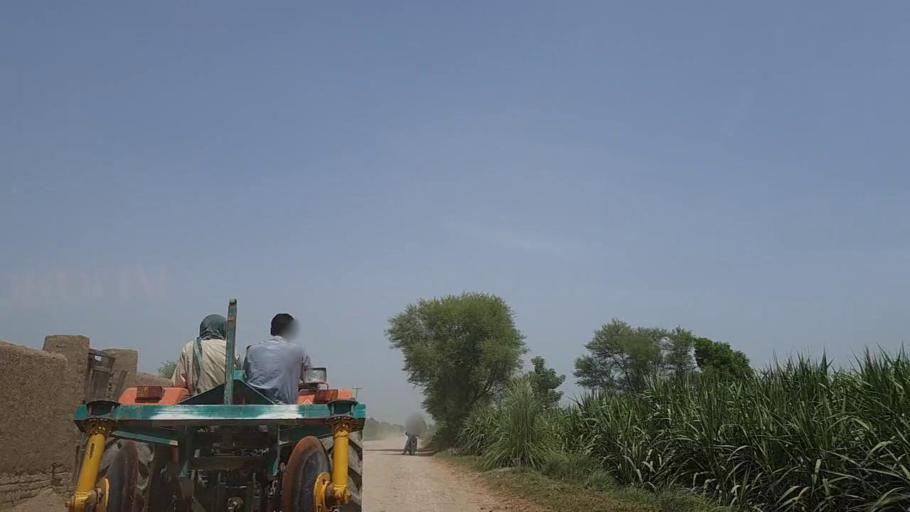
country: PK
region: Sindh
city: Tharu Shah
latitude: 26.8966
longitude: 68.0091
